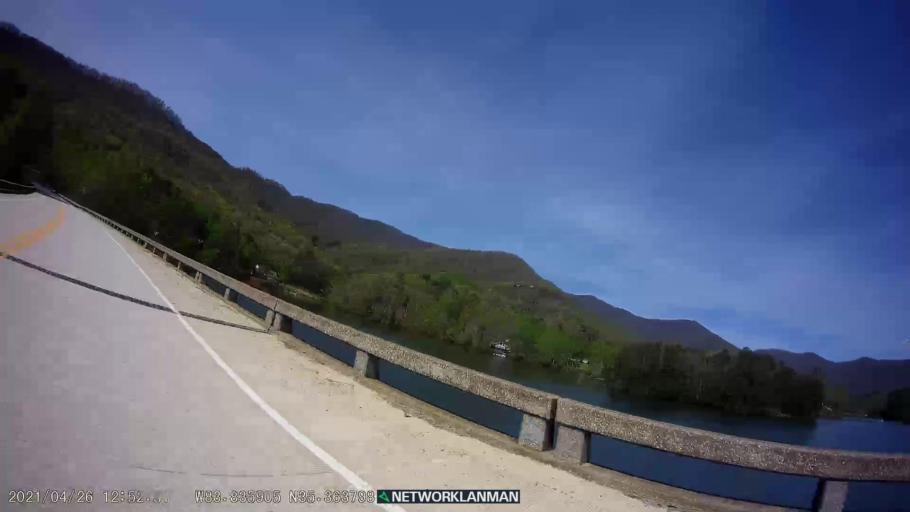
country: US
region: North Carolina
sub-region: Graham County
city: Robbinsville
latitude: 35.3621
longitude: -83.8353
